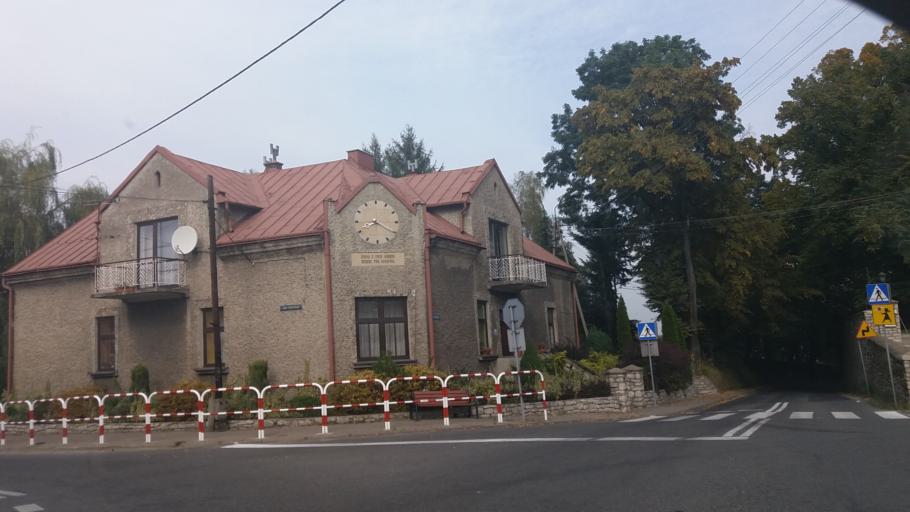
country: PL
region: Lesser Poland Voivodeship
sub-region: Powiat chrzanowski
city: Plaza
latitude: 50.0989
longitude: 19.4643
